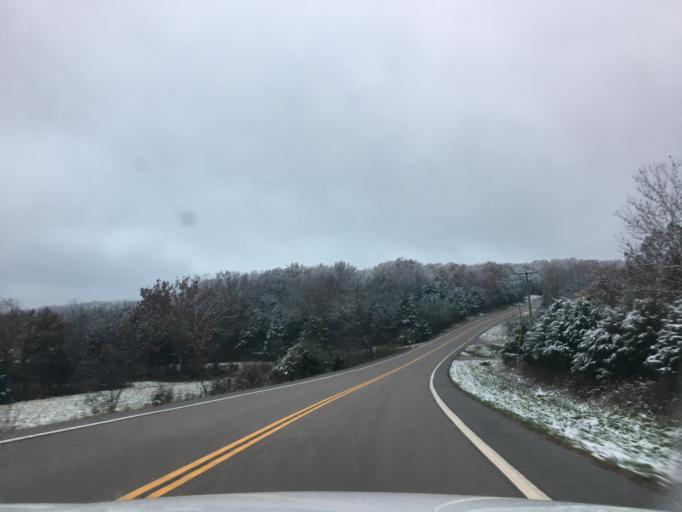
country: US
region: Missouri
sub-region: Osage County
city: Linn
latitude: 38.4682
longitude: -91.7722
